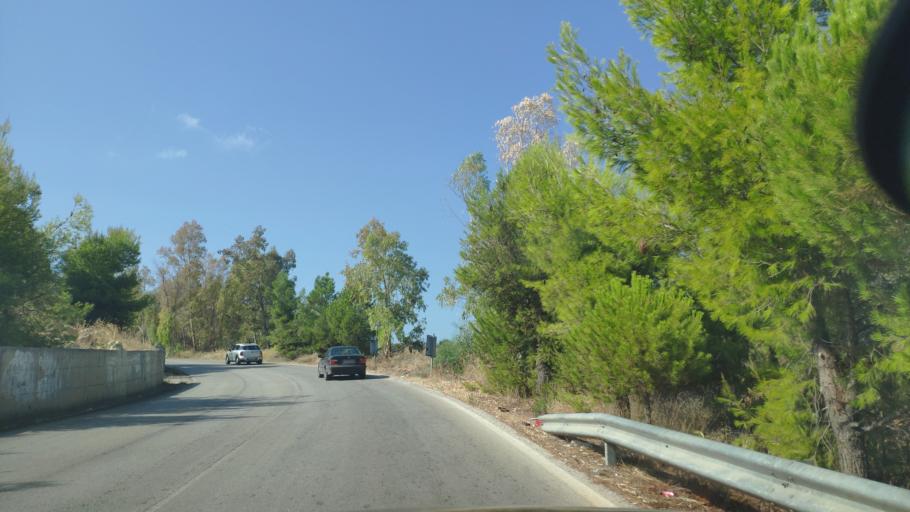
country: GR
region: Peloponnese
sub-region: Nomos Korinthias
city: Moulki
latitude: 37.9994
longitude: 22.7127
